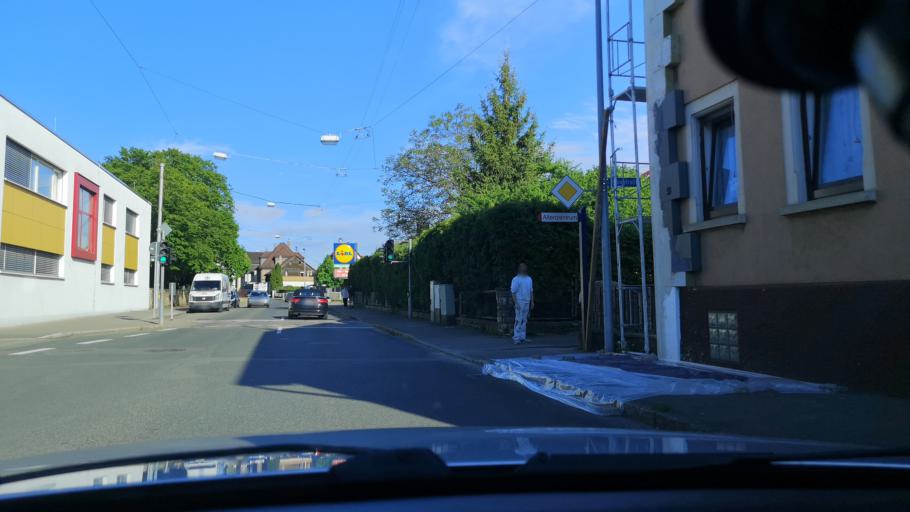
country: DE
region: Baden-Wuerttemberg
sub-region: Regierungsbezirk Stuttgart
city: Eislingen
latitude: 48.6978
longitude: 9.7101
